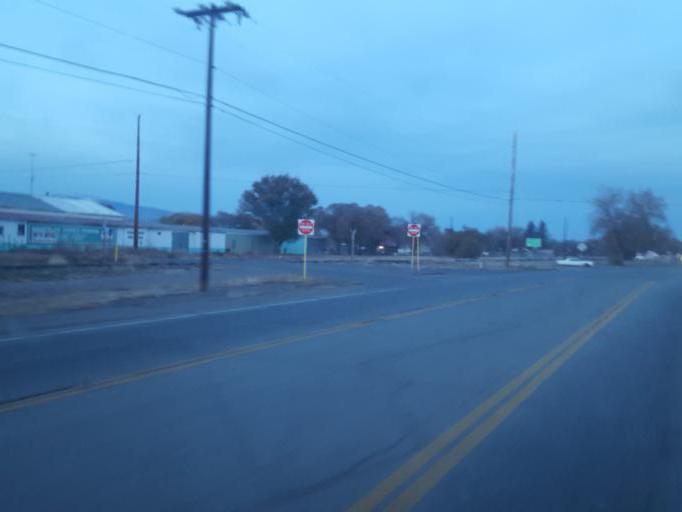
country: US
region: Colorado
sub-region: Rio Grande County
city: Monte Vista
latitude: 37.5750
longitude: -106.1303
